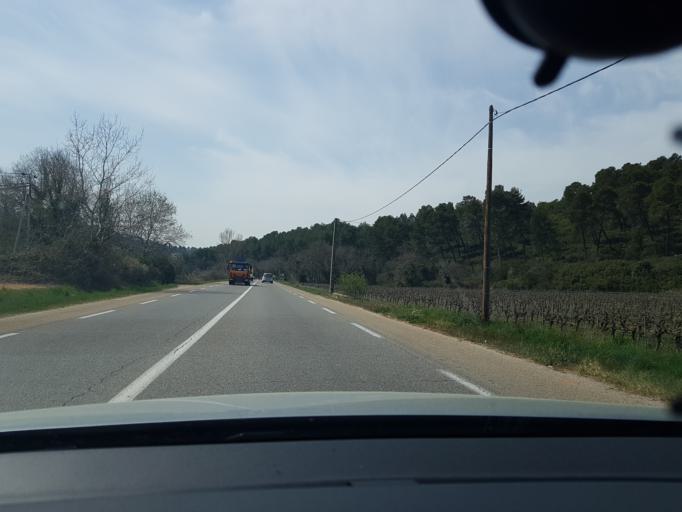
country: FR
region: Provence-Alpes-Cote d'Azur
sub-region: Departement des Bouches-du-Rhone
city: Gardanne
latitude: 43.4714
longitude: 5.4586
